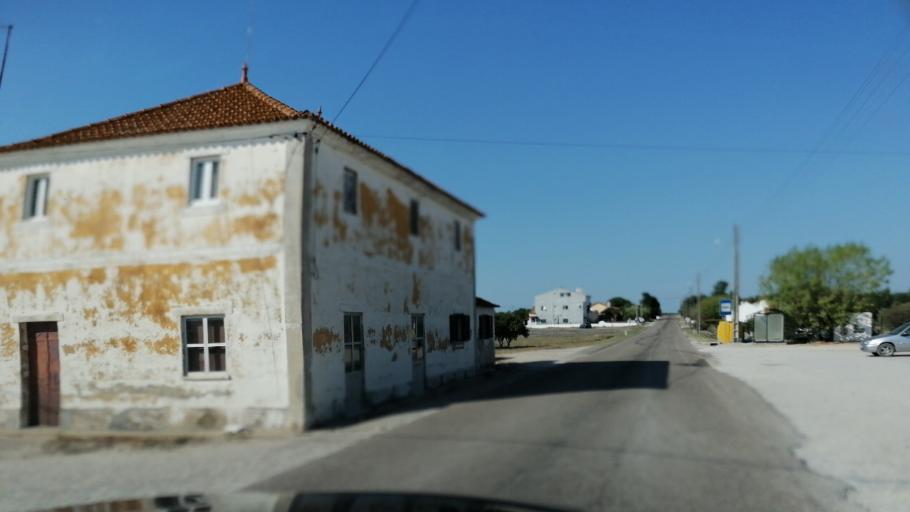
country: PT
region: Santarem
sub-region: Coruche
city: Coruche
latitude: 38.8246
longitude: -8.5657
